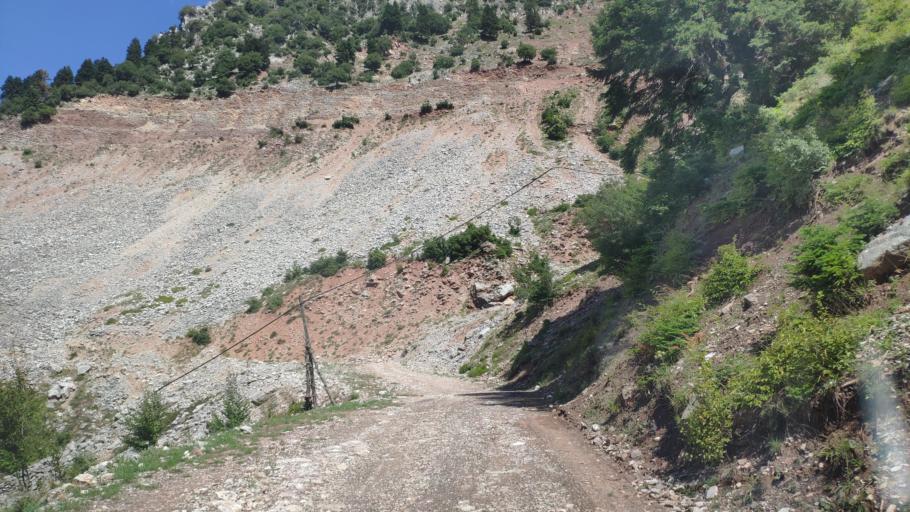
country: GR
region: Central Greece
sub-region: Nomos Evrytanias
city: Kerasochori
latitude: 39.1320
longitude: 21.6576
